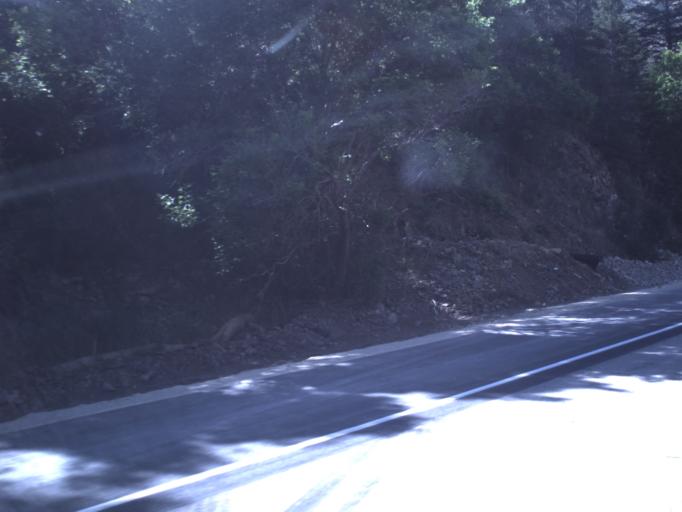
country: US
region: Utah
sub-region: Wasatch County
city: Heber
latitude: 40.3843
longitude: -111.3017
